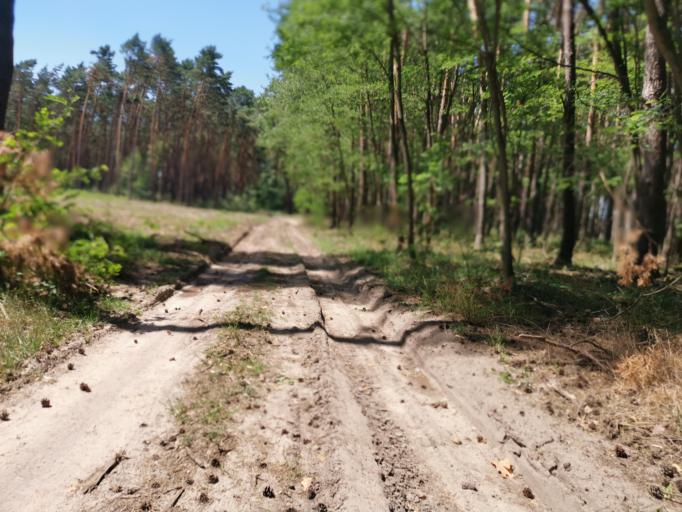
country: CZ
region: South Moravian
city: Vracov
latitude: 48.9661
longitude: 17.2375
